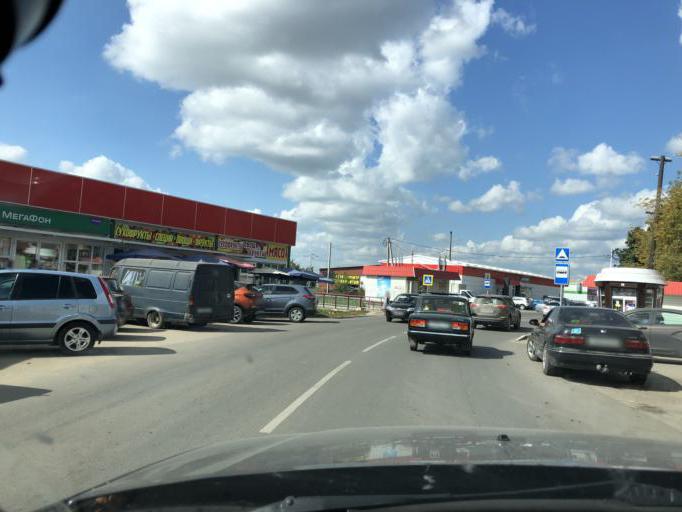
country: RU
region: Tula
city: Yasnogorsk
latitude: 54.4796
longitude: 37.6863
